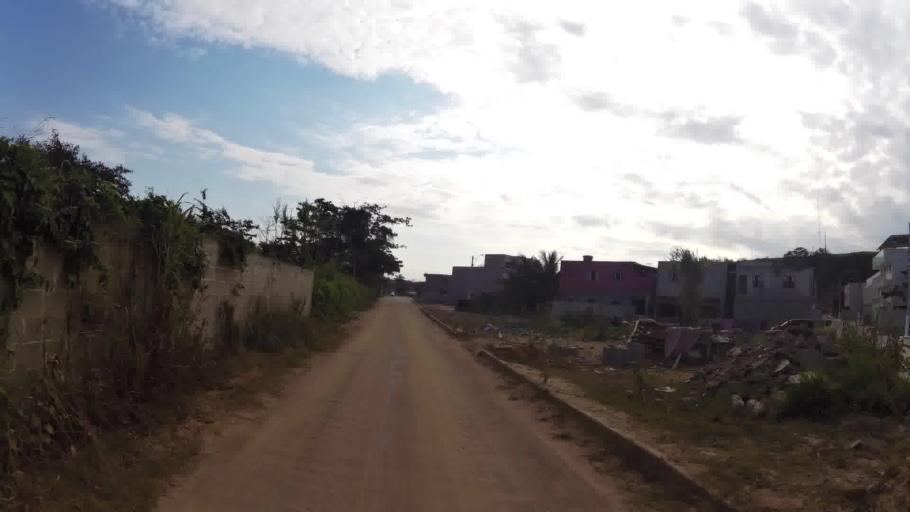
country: BR
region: Espirito Santo
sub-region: Itapemirim
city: Itapemirim
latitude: -21.0088
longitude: -40.8300
